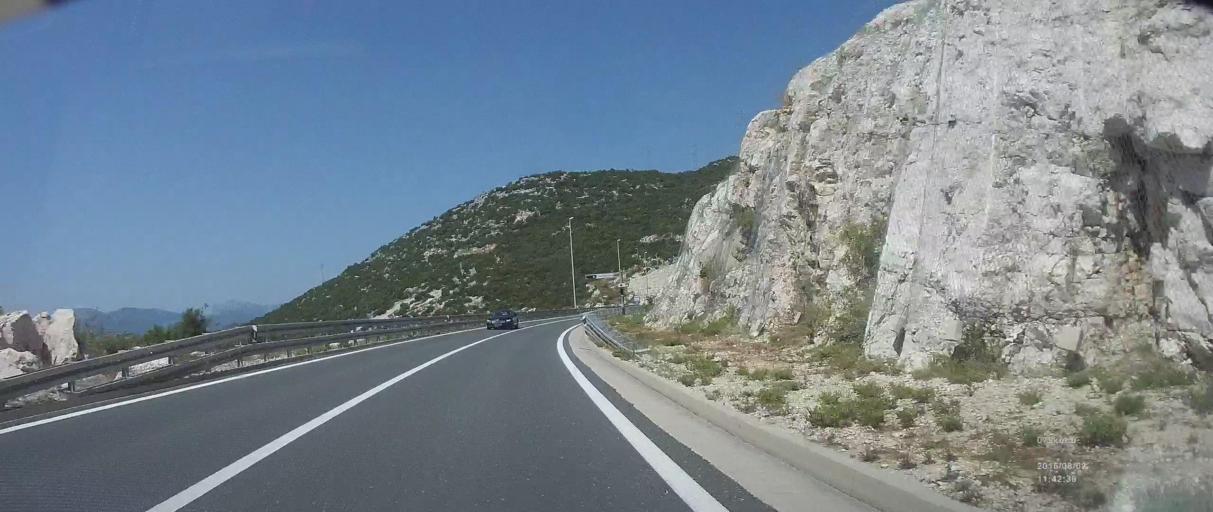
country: HR
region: Dubrovacko-Neretvanska
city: Komin
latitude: 43.0529
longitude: 17.4850
